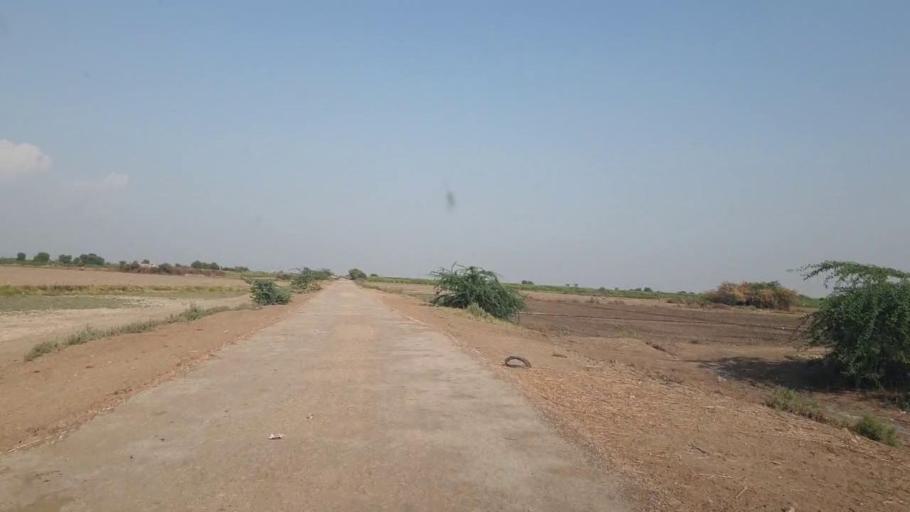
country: PK
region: Sindh
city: Sanghar
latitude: 26.0560
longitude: 68.8860
